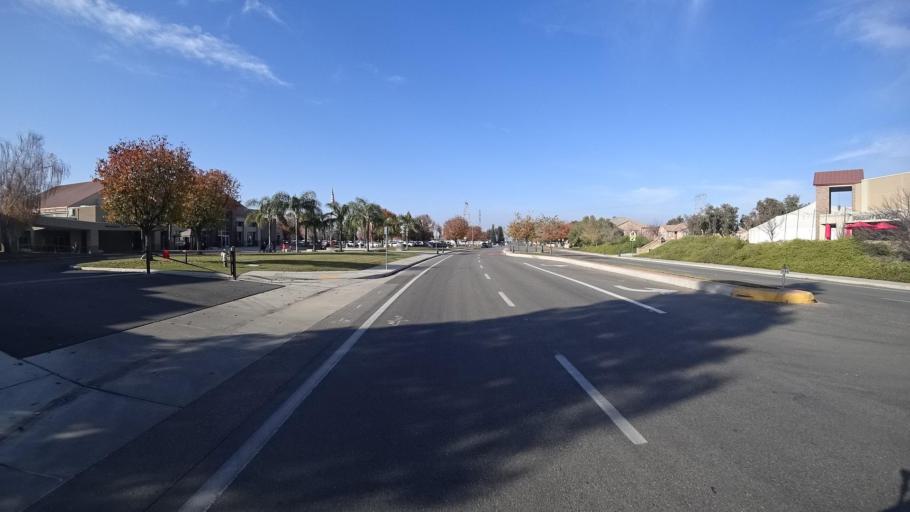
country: US
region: California
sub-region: Kern County
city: Bakersfield
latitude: 35.3979
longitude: -118.9178
